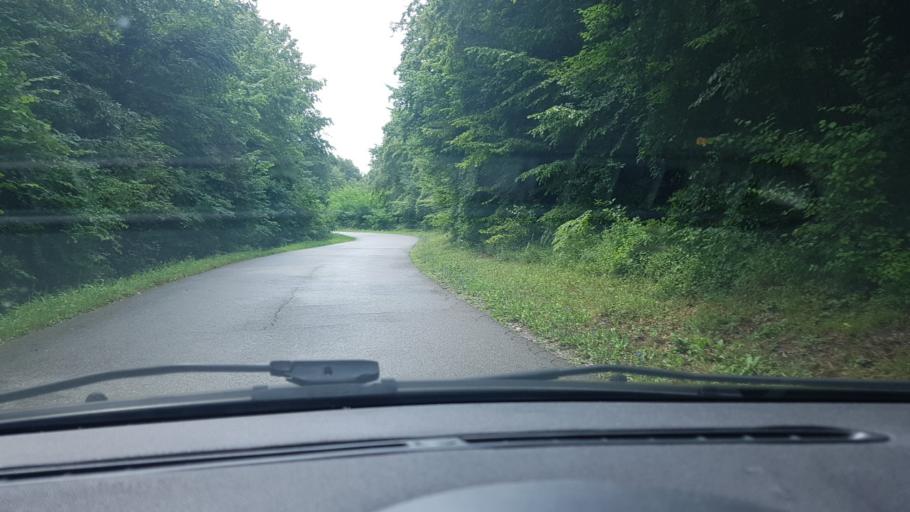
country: BA
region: Federation of Bosnia and Herzegovina
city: Trzacka Rastela
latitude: 44.9781
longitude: 15.6995
